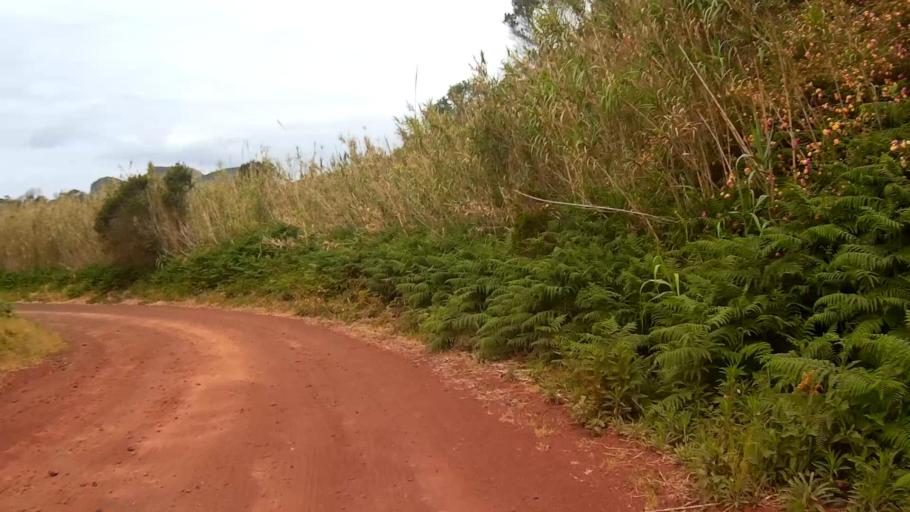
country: PT
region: Azores
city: Ribeira Grande
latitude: 38.5873
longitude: -28.8185
